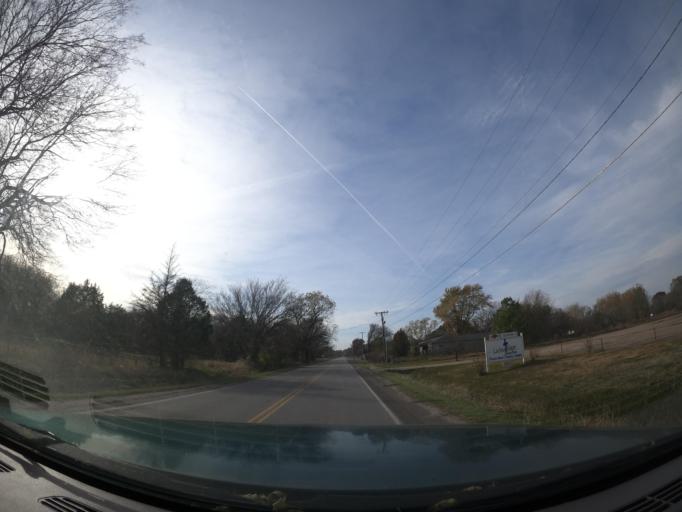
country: US
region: Oklahoma
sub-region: Tulsa County
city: Turley
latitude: 36.2496
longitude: -95.9631
